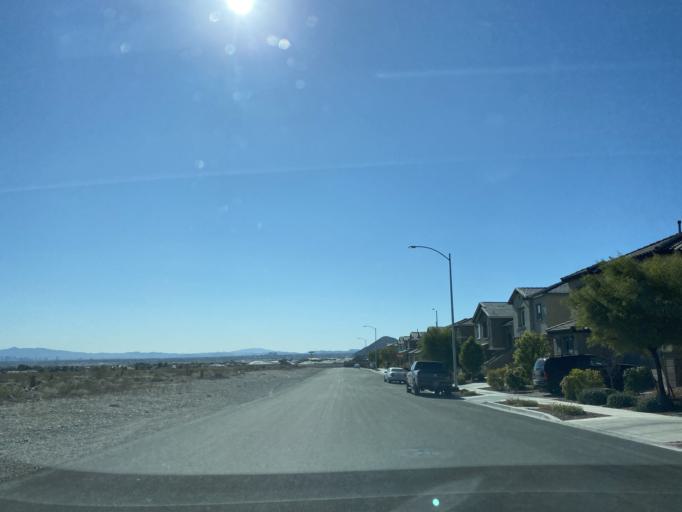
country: US
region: Nevada
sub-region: Clark County
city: Summerlin South
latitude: 36.2836
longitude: -115.3104
